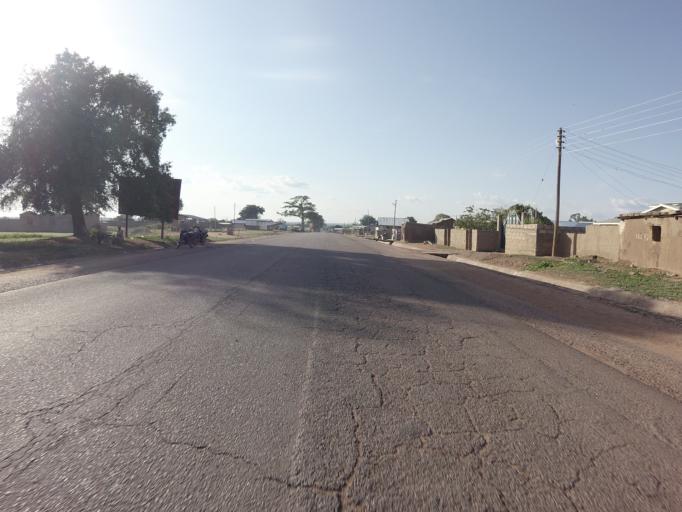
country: GH
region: Upper East
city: Navrongo
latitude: 10.9776
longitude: -1.1051
